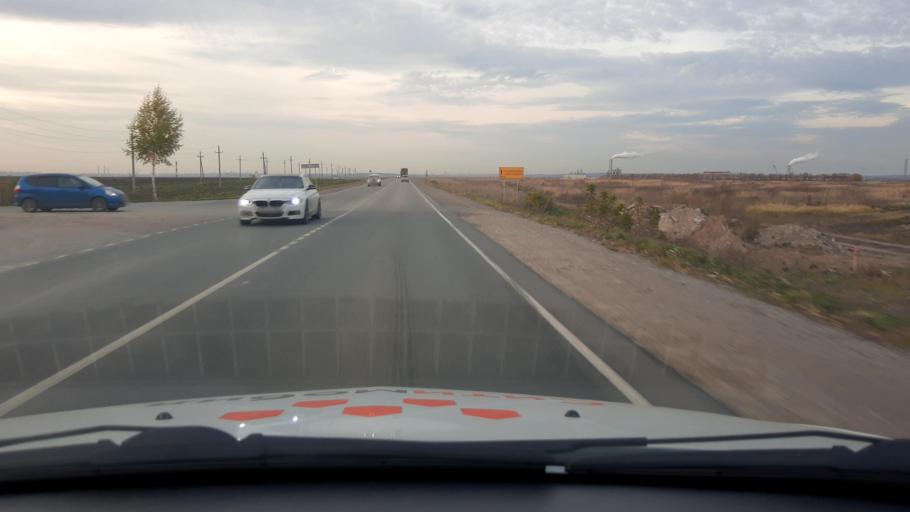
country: RU
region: Bashkortostan
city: Iglino
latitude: 54.7524
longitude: 56.2874
